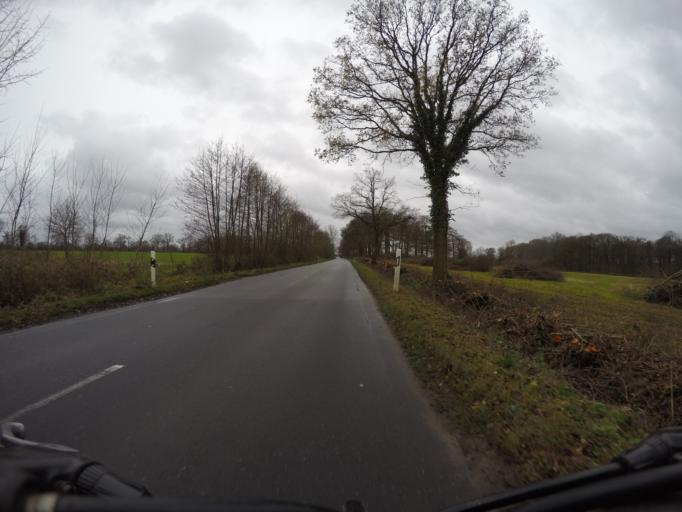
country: DE
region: Schleswig-Holstein
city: Hasloh
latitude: 53.6971
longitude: 9.8711
